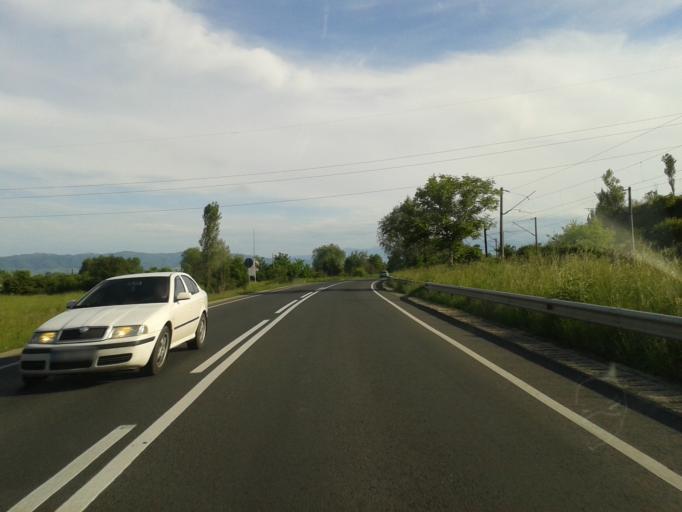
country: RO
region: Hunedoara
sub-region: Comuna Calan
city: Calan
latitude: 45.7512
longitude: 23.0010
